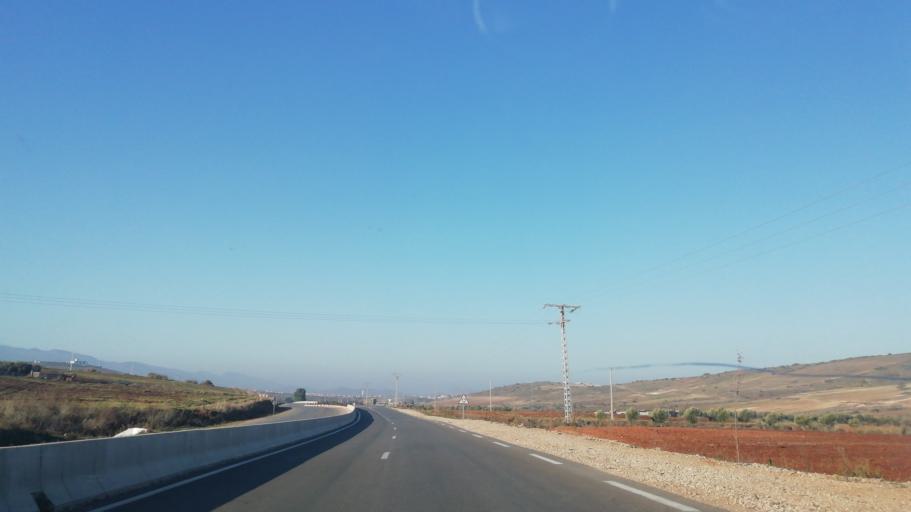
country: MA
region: Oriental
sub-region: Berkane-Taourirt
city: Ahfir
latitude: 34.9554
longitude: -2.0583
